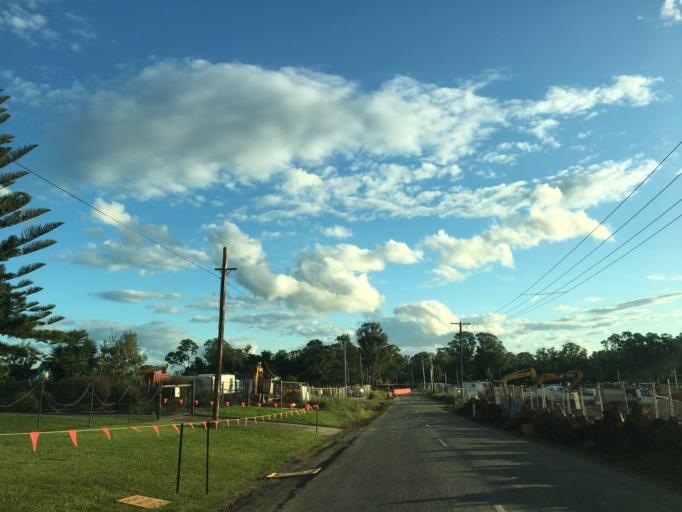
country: AU
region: New South Wales
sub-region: Campbelltown Municipality
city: Denham Court
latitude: -33.9690
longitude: 150.8073
